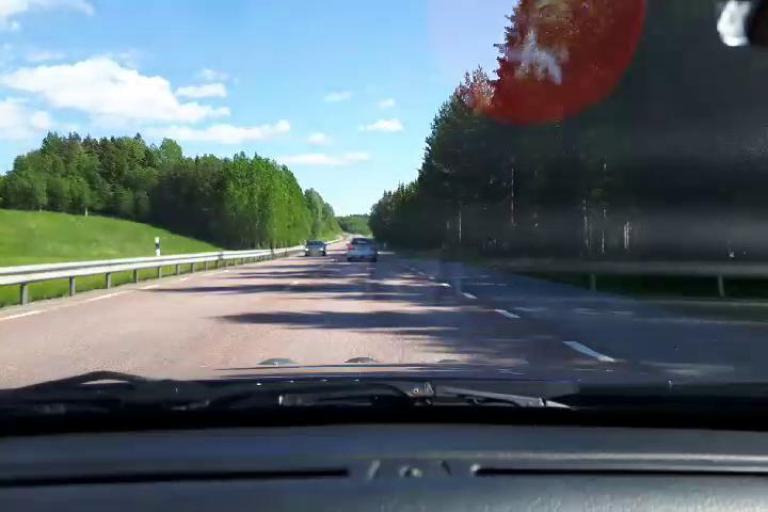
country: SE
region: Gaevleborg
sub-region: Hudiksvalls Kommun
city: Sorforsa
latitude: 61.7462
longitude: 16.8453
